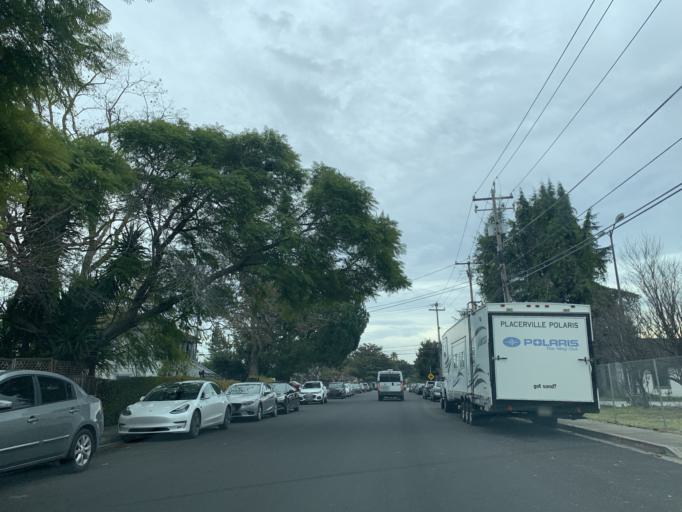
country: US
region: California
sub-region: Santa Clara County
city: Mountain View
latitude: 37.4075
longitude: -122.0729
